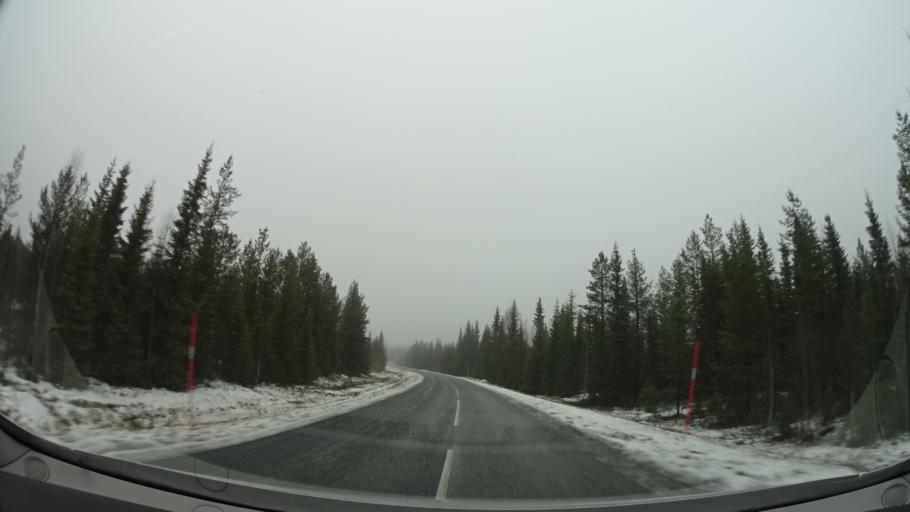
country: SE
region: Vaesterbotten
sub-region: Asele Kommun
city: Insjon
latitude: 64.3499
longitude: 17.8988
